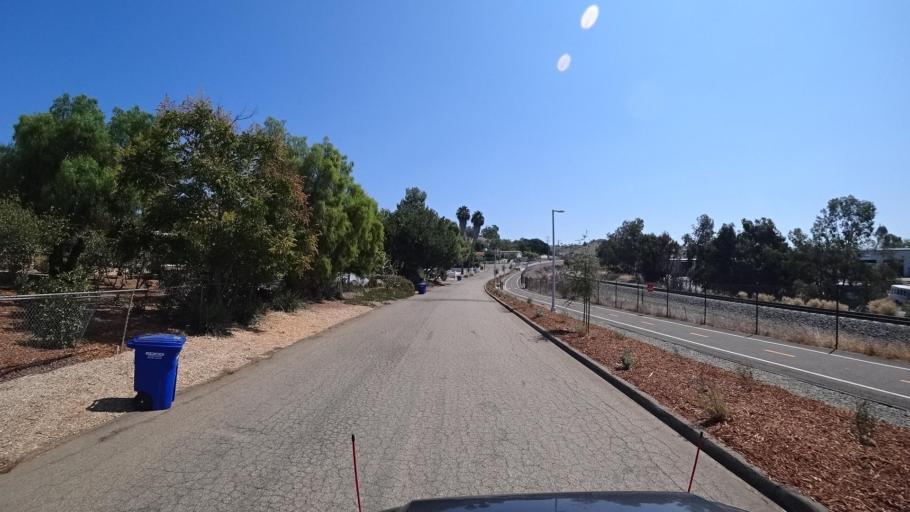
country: US
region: California
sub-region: San Diego County
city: Lake San Marcos
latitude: 33.1653
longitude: -117.2022
